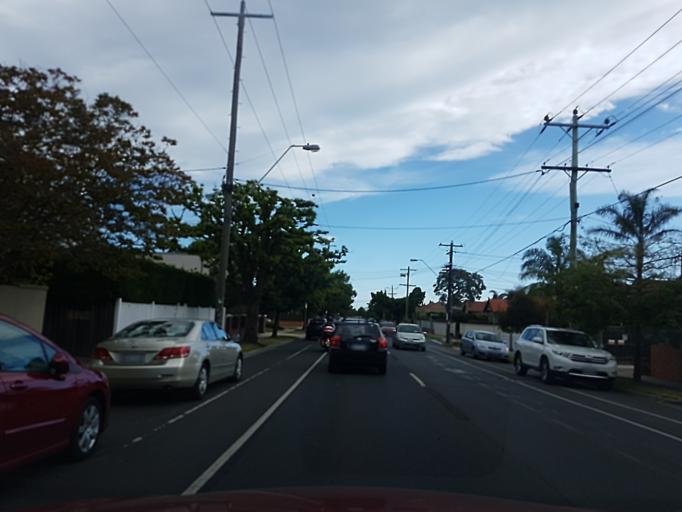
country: AU
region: Victoria
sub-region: Glen Eira
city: Caulfield
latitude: -37.8891
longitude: 145.0144
